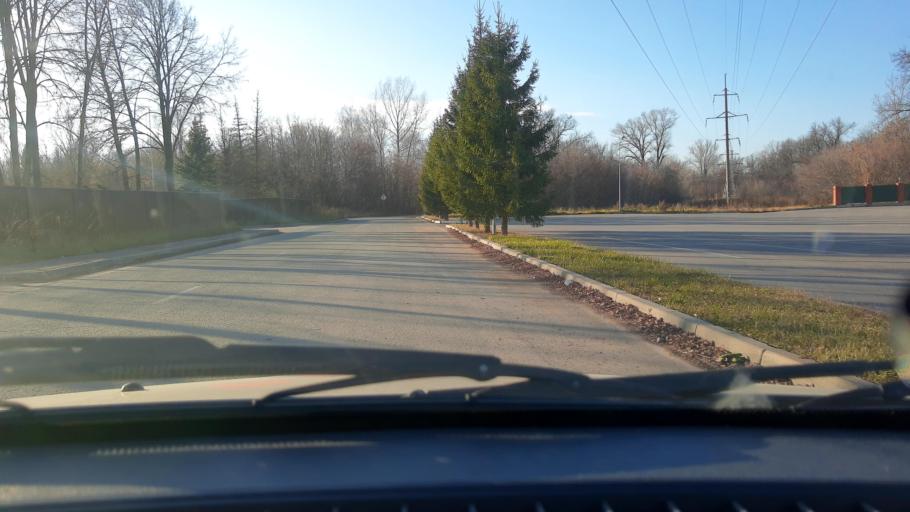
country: RU
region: Bashkortostan
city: Ufa
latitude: 54.6634
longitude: 55.9683
